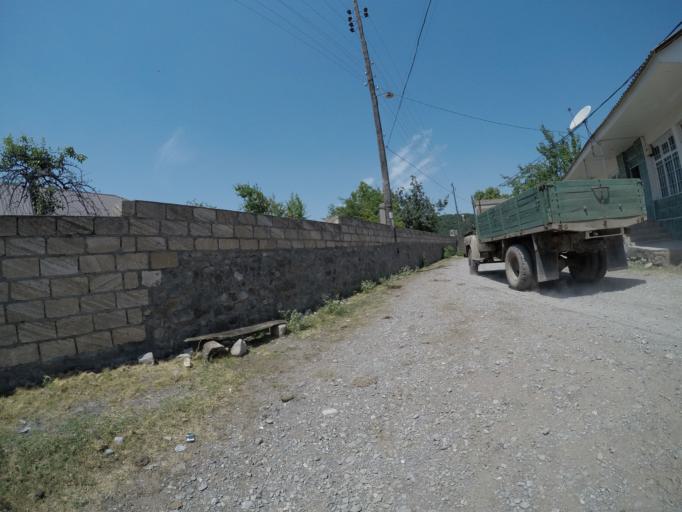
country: AZ
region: Qakh Rayon
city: Cinarli
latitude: 41.4830
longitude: 46.8488
